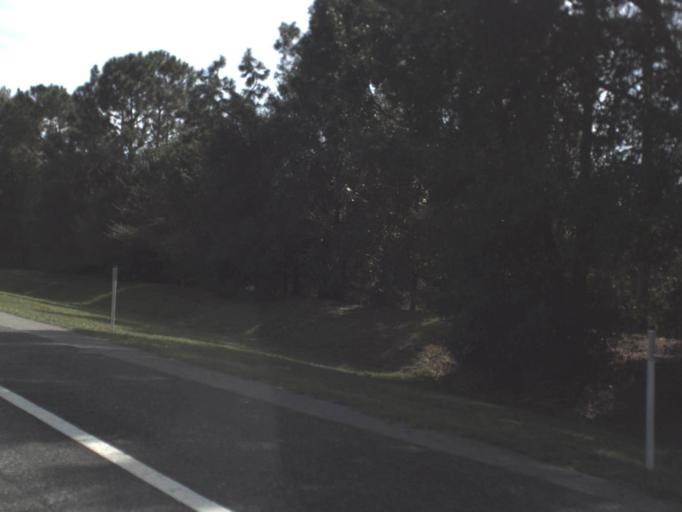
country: US
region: Florida
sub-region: Osceola County
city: Celebration
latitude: 28.3265
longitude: -81.5369
